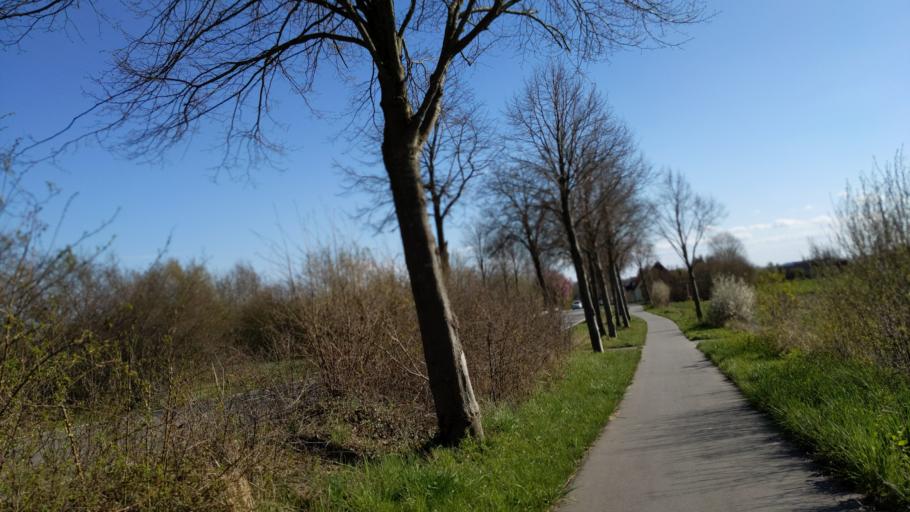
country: DE
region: Schleswig-Holstein
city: Eutin
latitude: 54.1111
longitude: 10.6108
